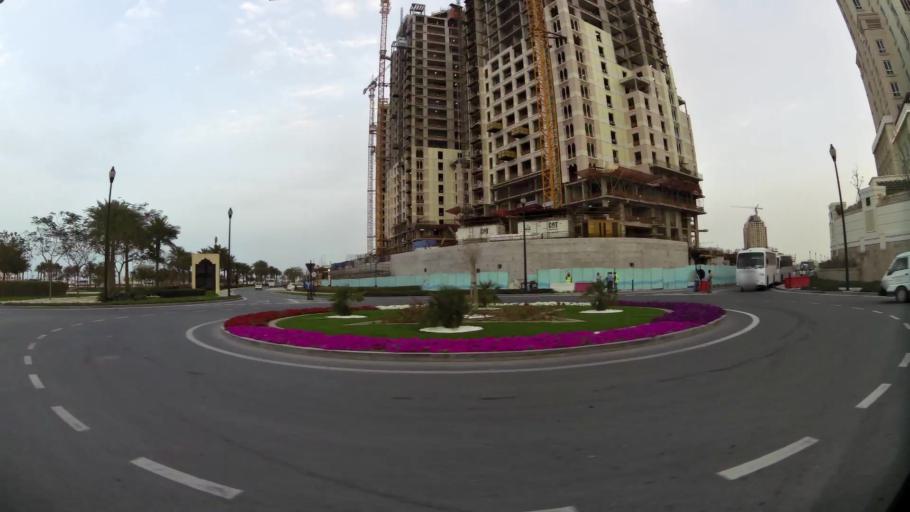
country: QA
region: Baladiyat ad Dawhah
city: Doha
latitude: 25.3712
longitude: 51.5572
